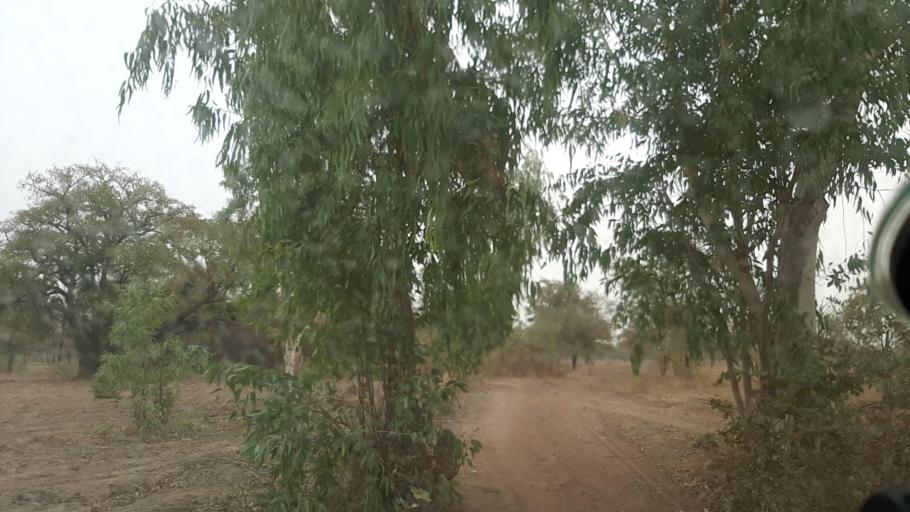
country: BF
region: Boucle du Mouhoun
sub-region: Province des Banwa
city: Salanso
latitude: 11.8515
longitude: -4.4270
